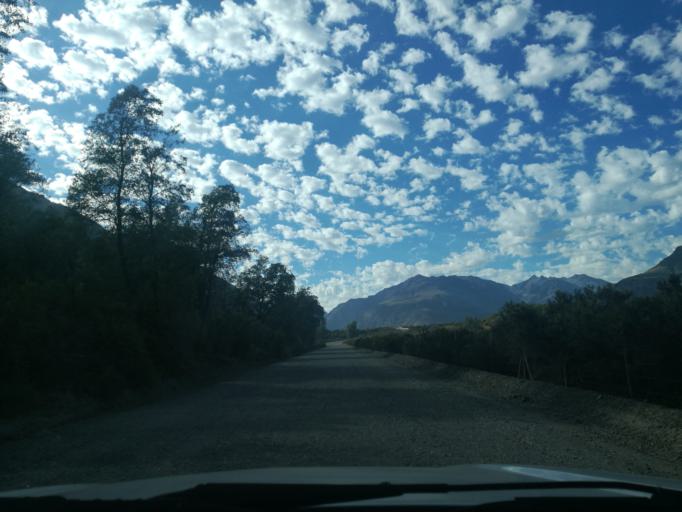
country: CL
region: O'Higgins
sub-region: Provincia de Cachapoal
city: Machali
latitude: -34.2909
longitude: -70.4357
